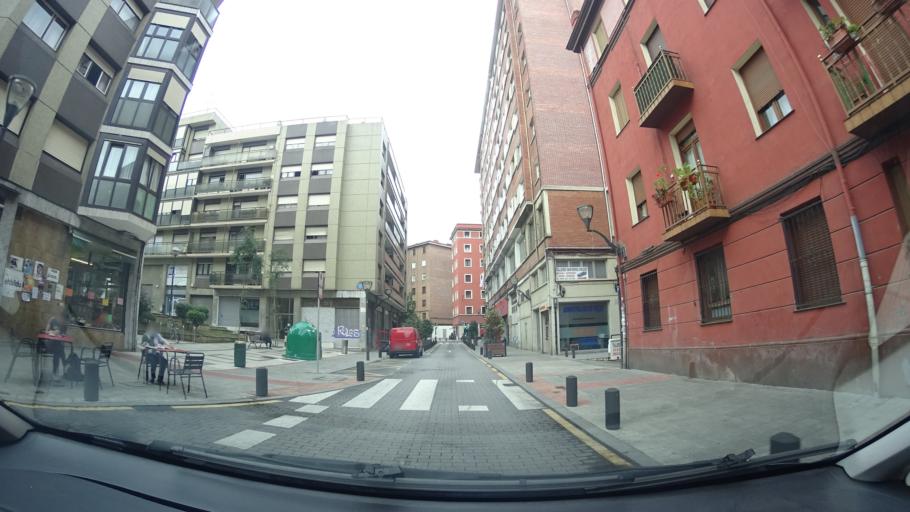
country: ES
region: Basque Country
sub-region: Bizkaia
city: Bilbao
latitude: 43.2533
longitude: -2.9326
